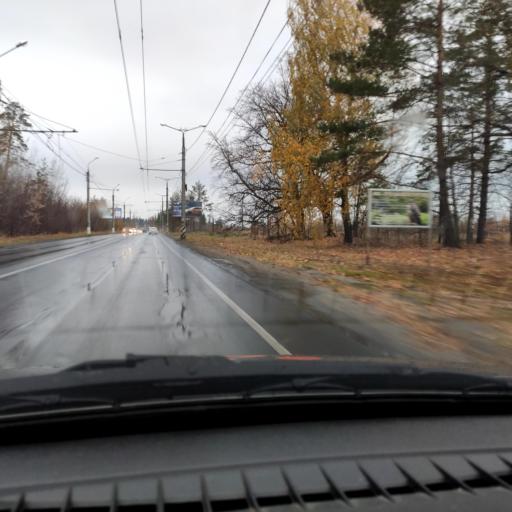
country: RU
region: Samara
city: Tol'yatti
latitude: 53.4888
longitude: 49.3839
